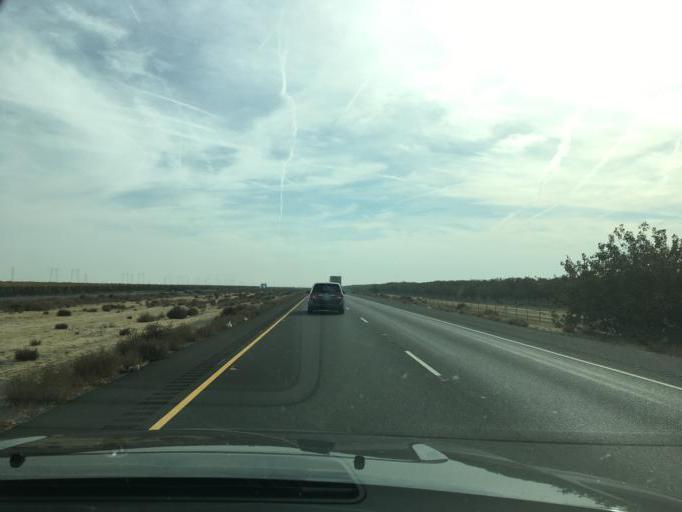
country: US
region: California
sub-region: Kings County
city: Kettleman City
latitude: 35.9152
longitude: -119.8925
